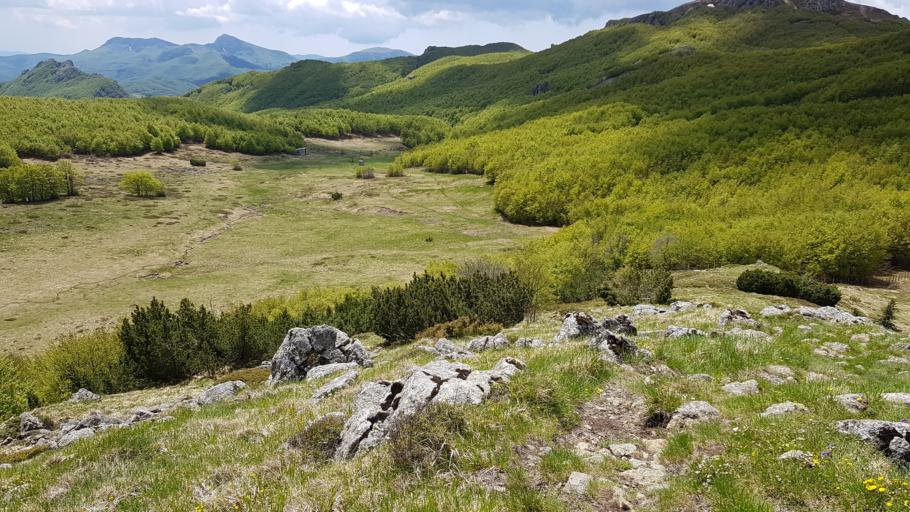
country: IT
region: Liguria
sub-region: Provincia di Genova
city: Santo Stefano d'Aveto
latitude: 44.5576
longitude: 9.4996
